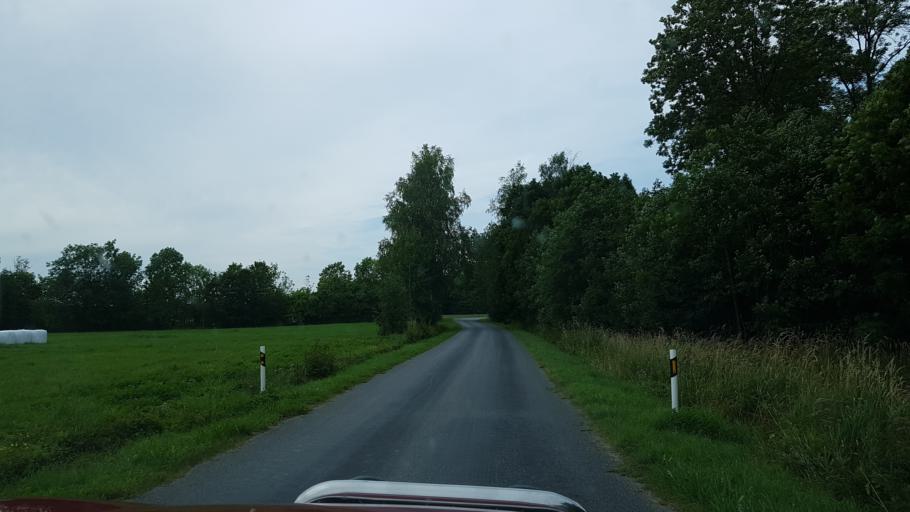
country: EE
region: Laeaene
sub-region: Ridala Parish
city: Uuemoisa
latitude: 59.0164
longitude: 23.7207
